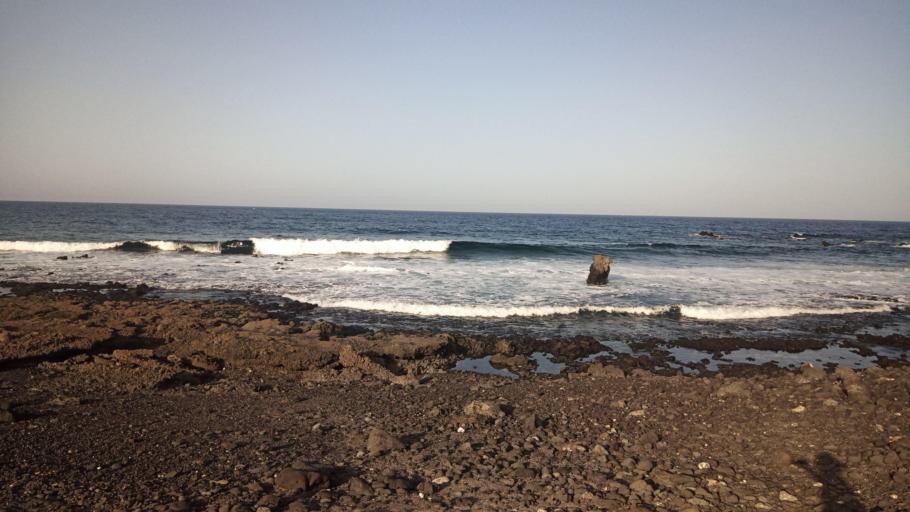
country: ES
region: Canary Islands
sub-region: Provincia de Las Palmas
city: Haria
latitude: 29.2086
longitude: -13.4262
